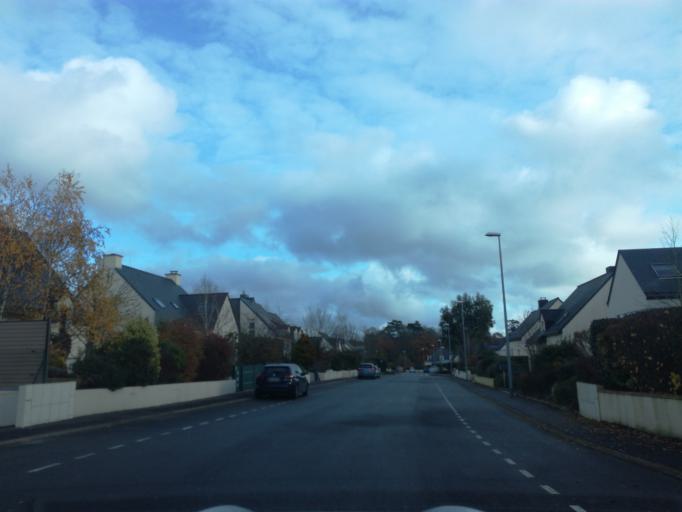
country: FR
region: Brittany
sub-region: Departement d'Ille-et-Vilaine
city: Cesson-Sevigne
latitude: 48.1106
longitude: -1.6059
